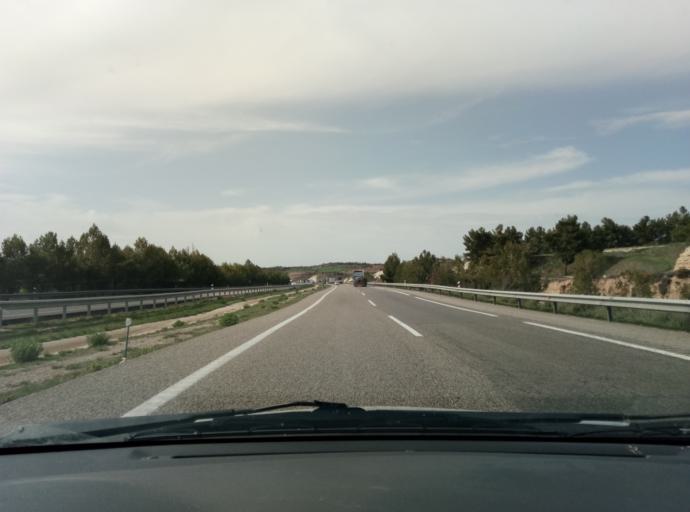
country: ES
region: Catalonia
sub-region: Provincia de Lleida
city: Cervera
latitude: 41.6564
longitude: 1.3122
